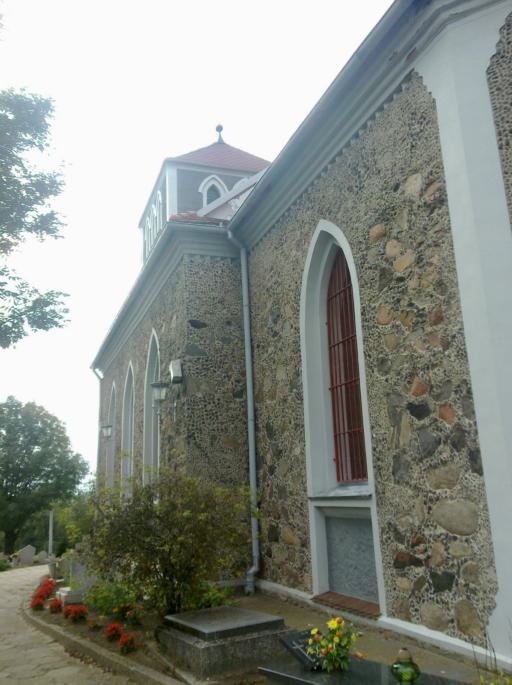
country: PL
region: Kujawsko-Pomorskie
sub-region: Powiat swiecki
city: Bukowiec
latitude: 53.4290
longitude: 18.3086
